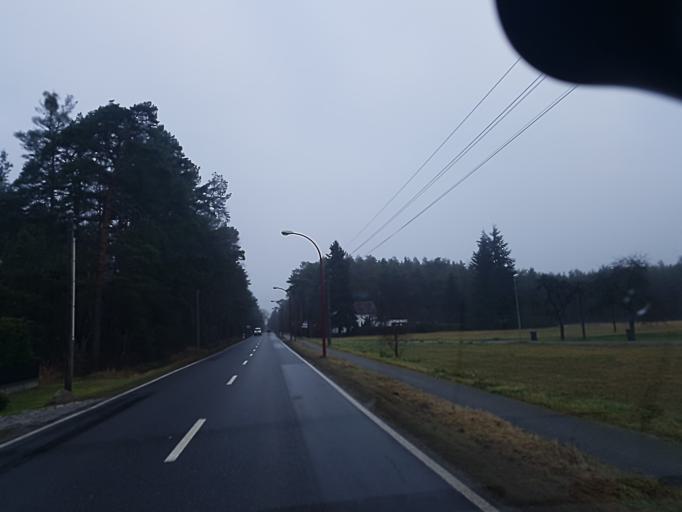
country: DE
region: Brandenburg
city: Finsterwalde
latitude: 51.5896
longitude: 13.7053
